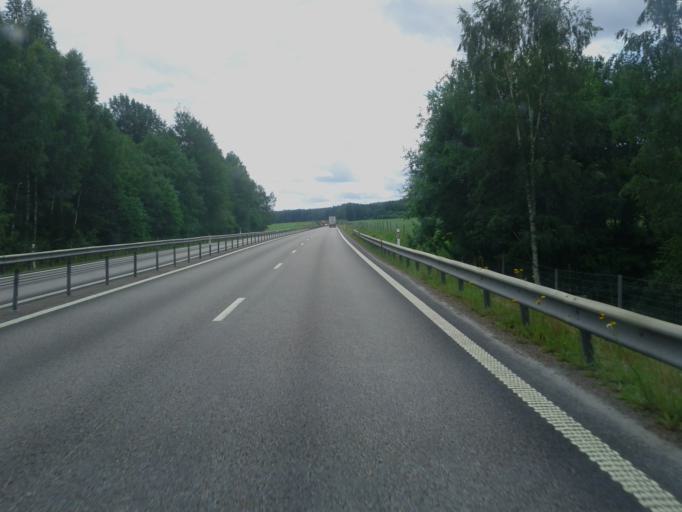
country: SE
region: Dalarna
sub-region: Borlange Kommun
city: Ornas
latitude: 60.4019
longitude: 15.6131
